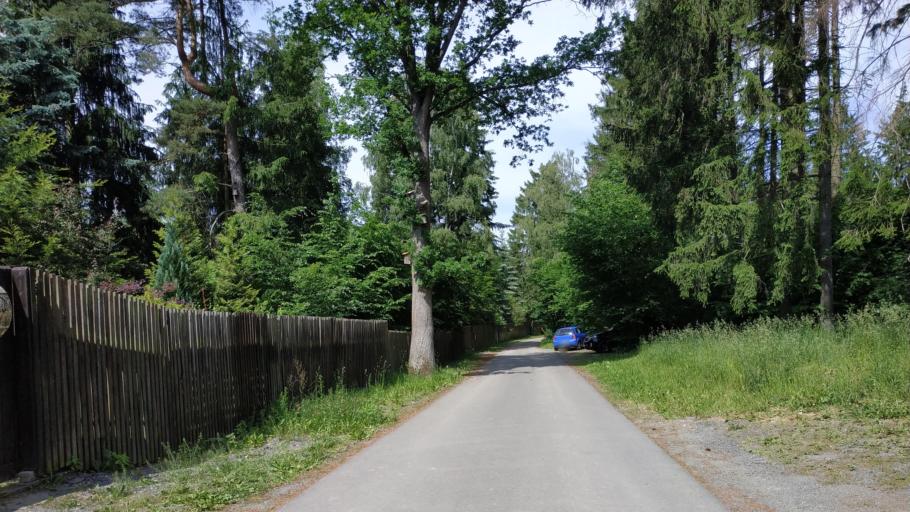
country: DE
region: Saxony
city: Plauen
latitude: 50.5333
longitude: 12.1198
